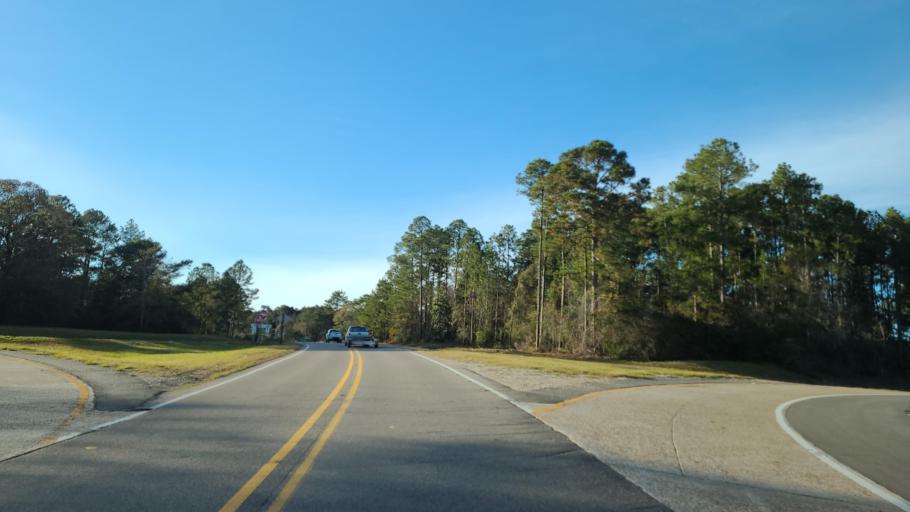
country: US
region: Mississippi
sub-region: Lamar County
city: Purvis
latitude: 31.1393
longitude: -89.3668
